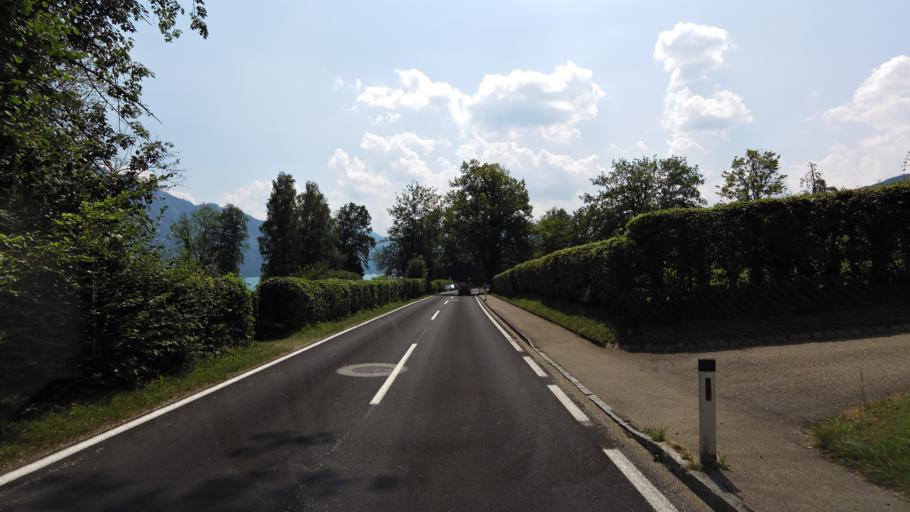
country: AT
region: Upper Austria
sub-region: Politischer Bezirk Vocklabruck
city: Steinbach am Attersee
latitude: 47.8481
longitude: 13.5263
